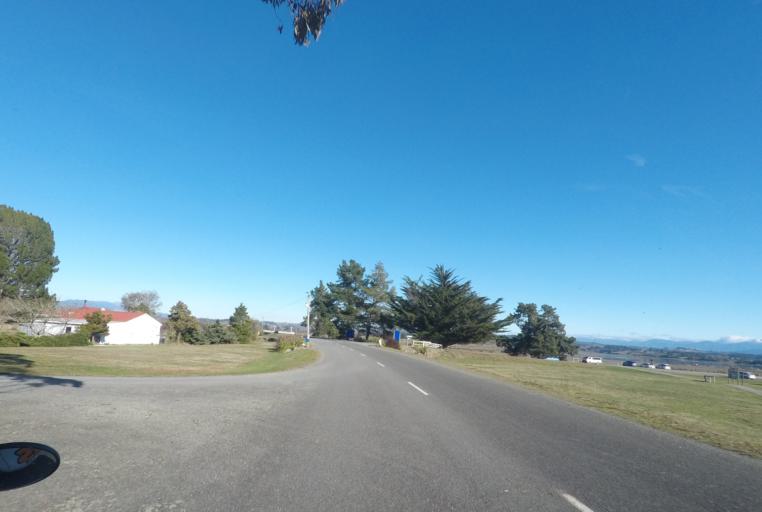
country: NZ
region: Tasman
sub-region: Tasman District
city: Mapua
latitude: -41.2824
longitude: 173.1339
